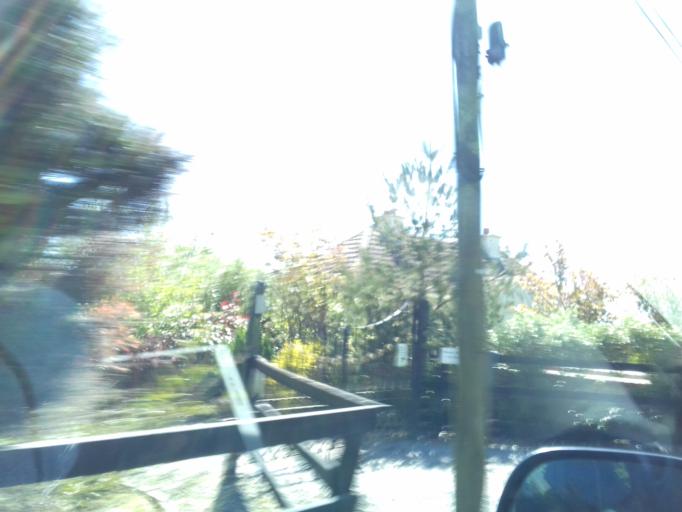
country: IE
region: Munster
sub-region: Waterford
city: Dunmore East
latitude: 52.1643
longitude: -6.8861
